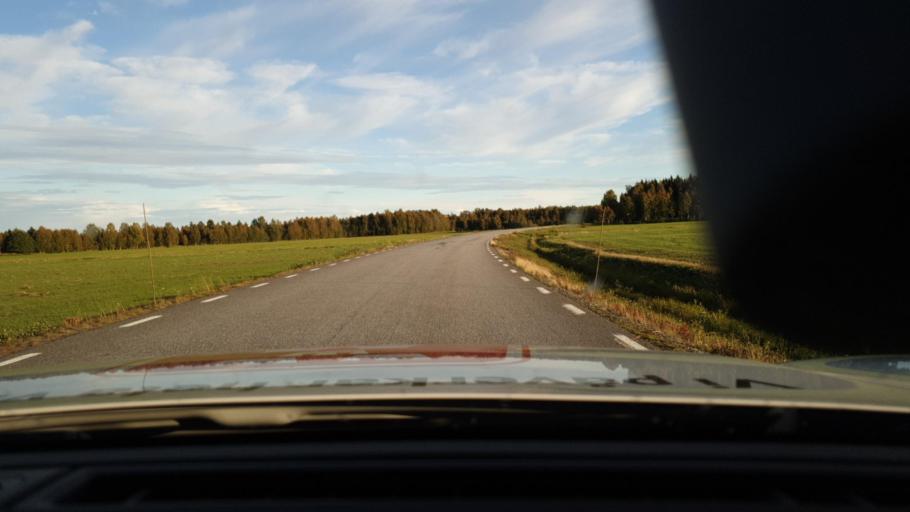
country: SE
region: Norrbotten
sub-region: Kalix Kommun
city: Toere
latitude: 65.8828
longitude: 22.6630
